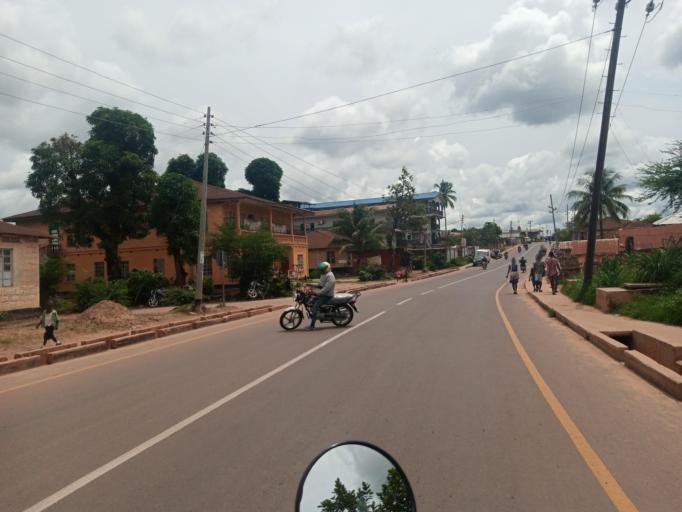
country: SL
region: Southern Province
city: Bo
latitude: 7.9572
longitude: -11.7305
